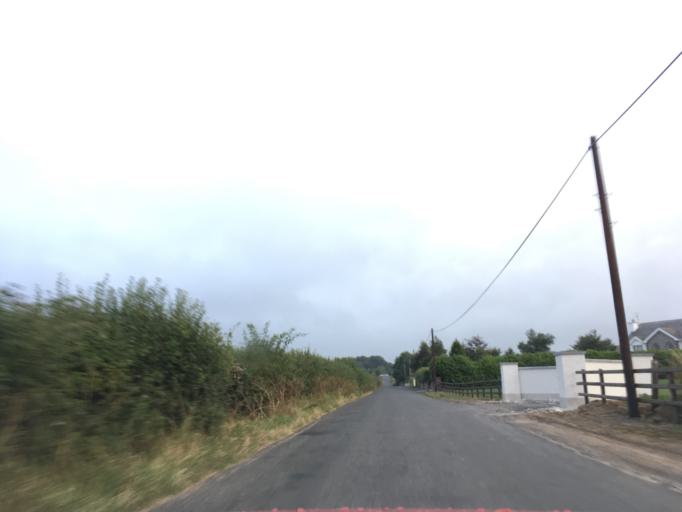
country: IE
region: Munster
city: Cashel
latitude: 52.4834
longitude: -7.9774
